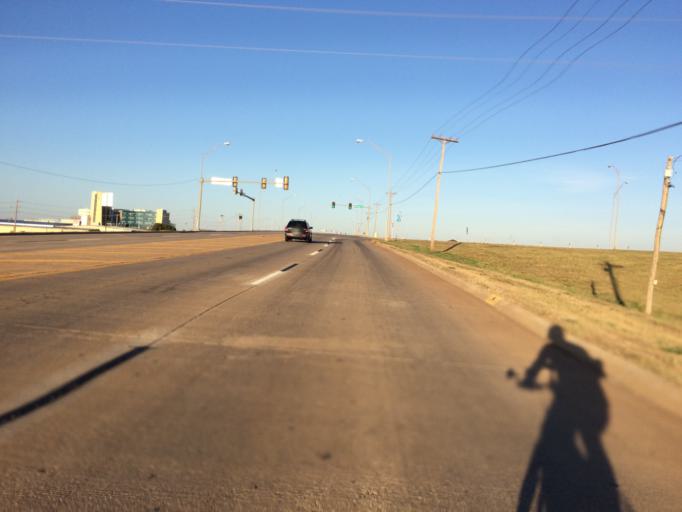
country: US
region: Oklahoma
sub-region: Cleveland County
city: Norman
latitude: 35.2621
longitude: -97.4823
